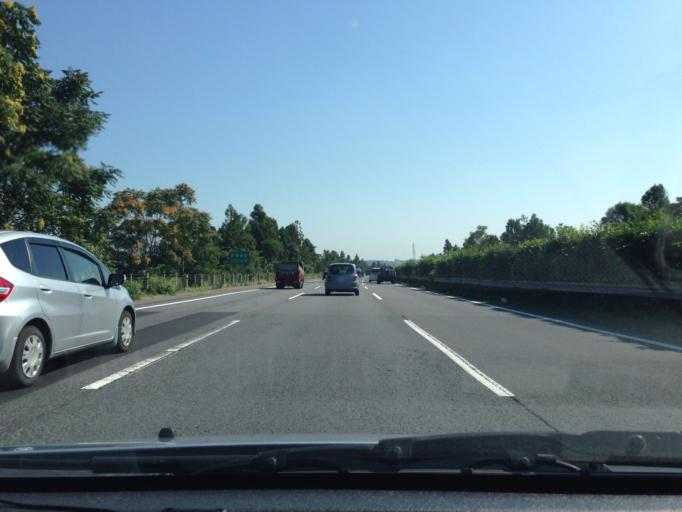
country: JP
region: Ibaraki
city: Naka
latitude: 36.0871
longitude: 140.1569
